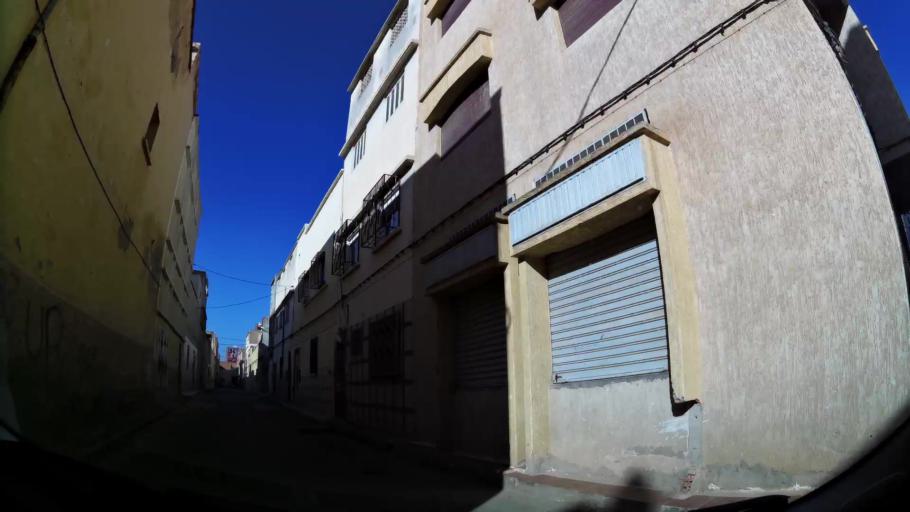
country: MA
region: Oriental
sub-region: Oujda-Angad
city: Oujda
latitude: 34.6887
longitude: -1.9111
